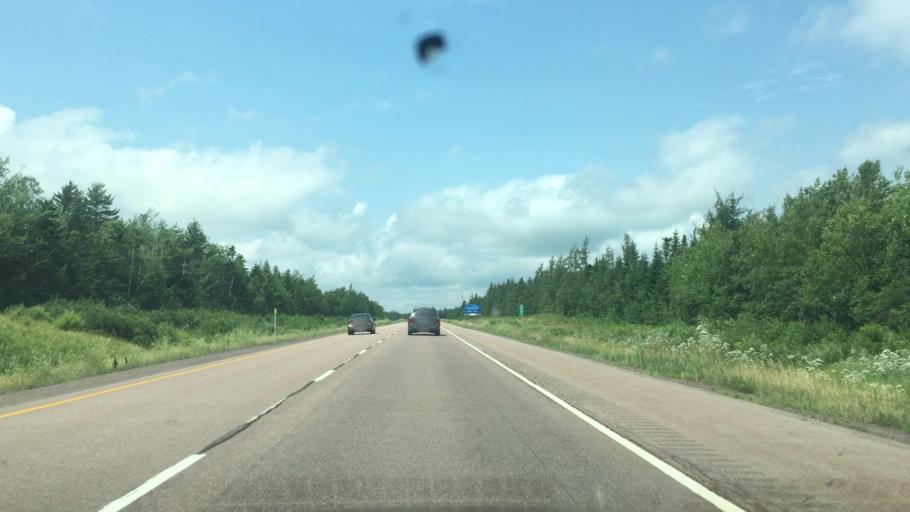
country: CA
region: New Brunswick
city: Sackville
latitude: 45.9893
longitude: -64.4832
